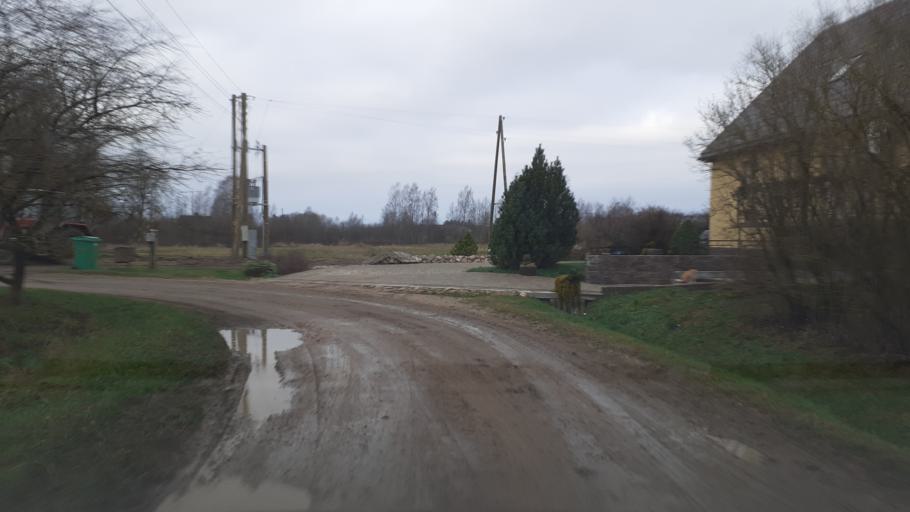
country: LV
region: Aizpute
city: Aizpute
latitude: 56.8029
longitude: 21.6679
